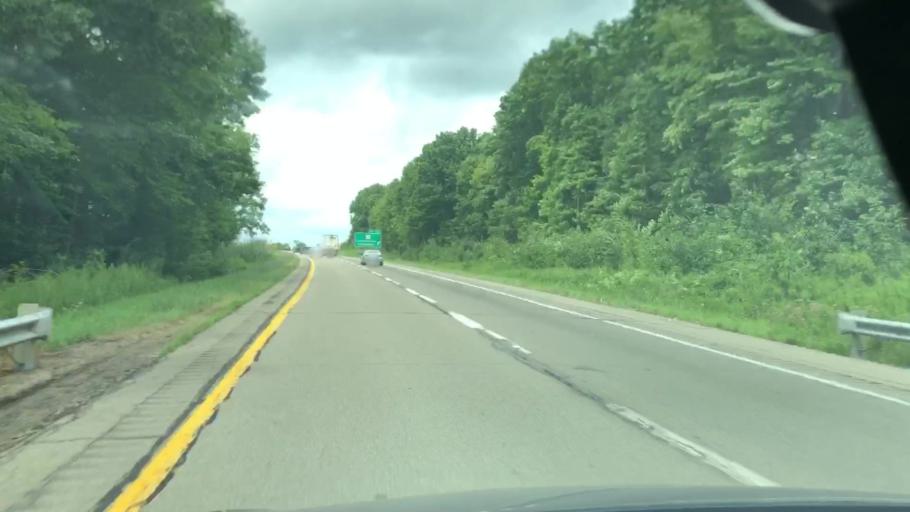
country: US
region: Pennsylvania
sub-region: Crawford County
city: Meadville
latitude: 41.7108
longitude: -80.1984
